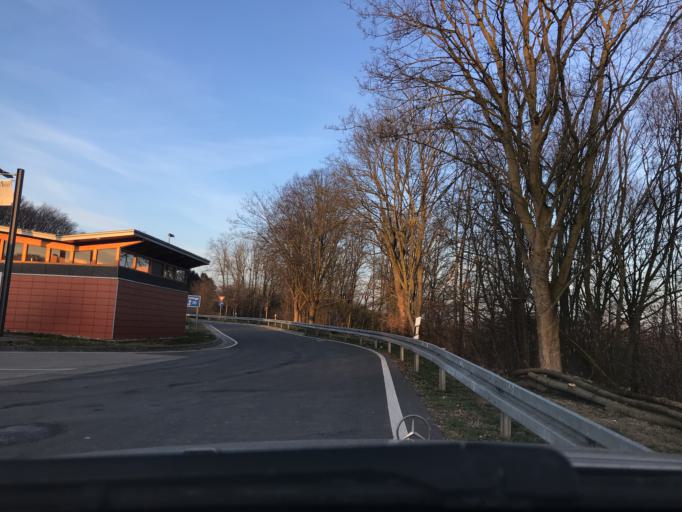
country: DE
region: North Rhine-Westphalia
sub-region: Regierungsbezirk Arnsberg
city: Frondenberg
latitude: 51.5254
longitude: 7.7917
